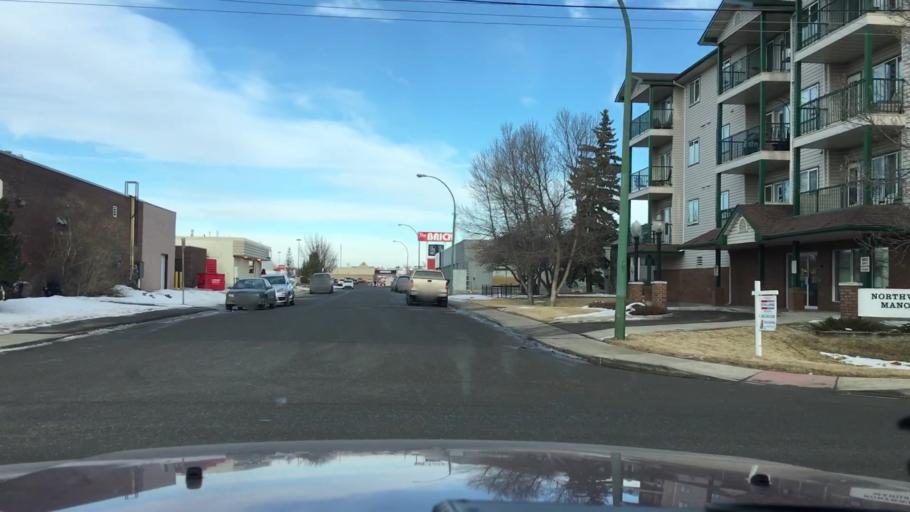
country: CA
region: Saskatchewan
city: Regina
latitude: 50.4789
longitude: -104.6165
